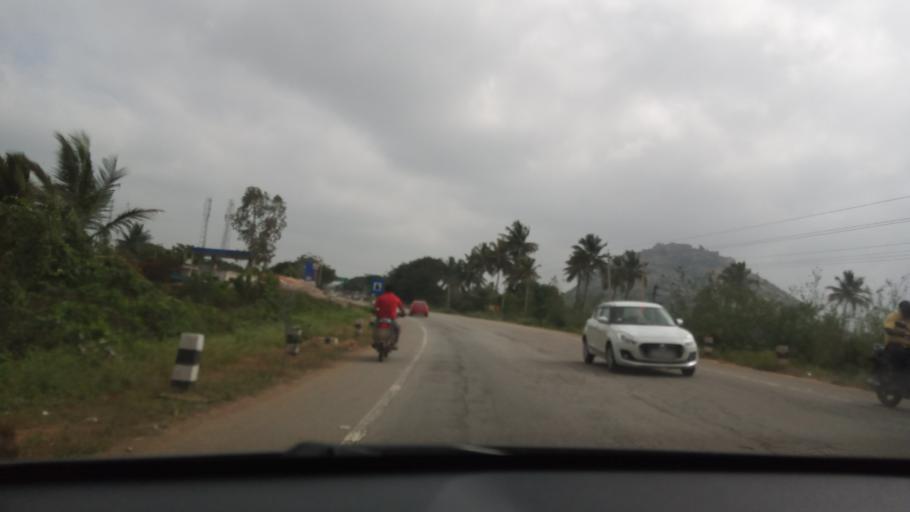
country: IN
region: Karnataka
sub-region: Chikkaballapur
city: Chintamani
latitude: 13.3248
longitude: 77.9894
